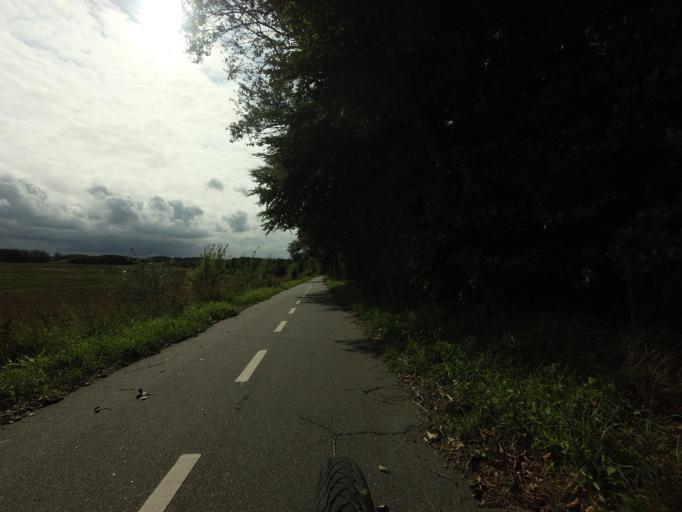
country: DK
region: North Denmark
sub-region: Hjorring Kommune
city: Hjorring
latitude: 57.5092
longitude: 10.0108
